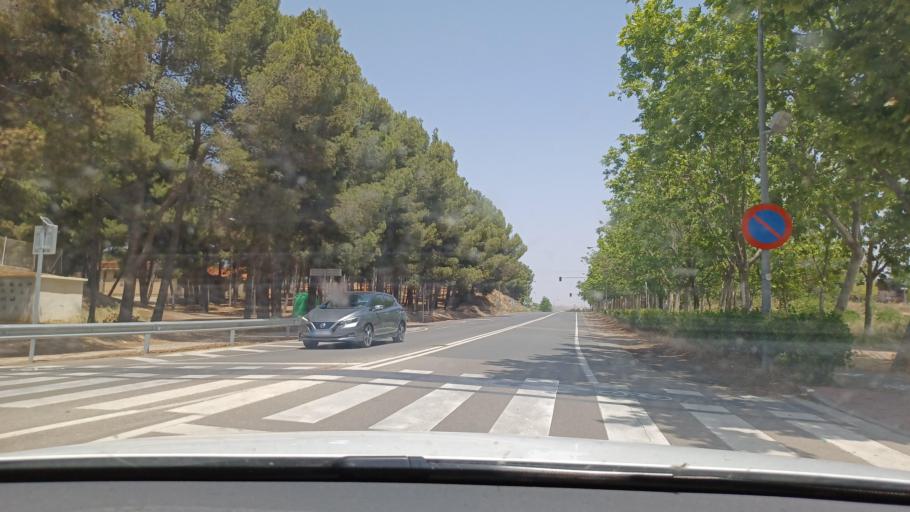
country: ES
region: Navarre
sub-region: Provincia de Navarra
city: Tudela
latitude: 42.0530
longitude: -1.6120
